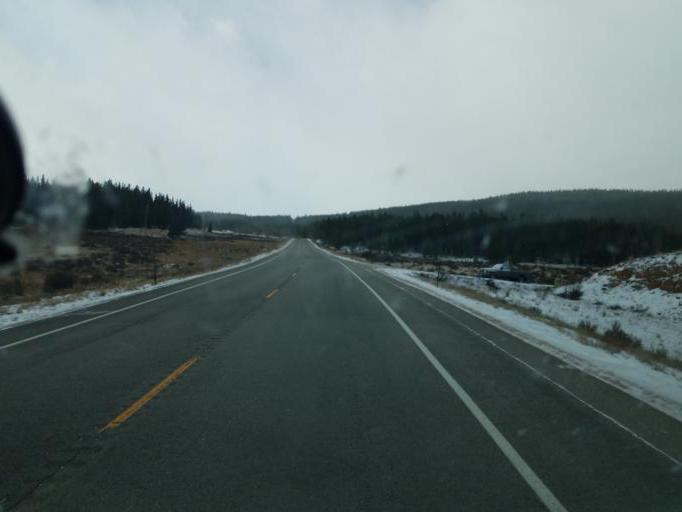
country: US
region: Colorado
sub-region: Summit County
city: Breckenridge
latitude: 39.4262
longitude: -105.7649
